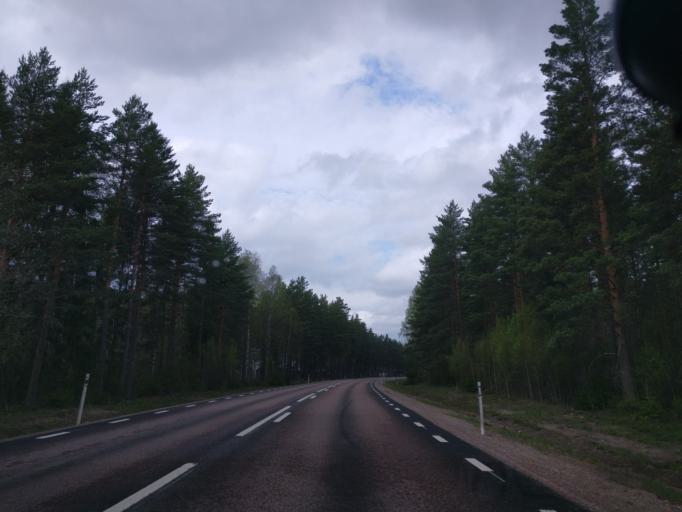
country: SE
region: Vaermland
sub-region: Hagfors Kommun
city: Ekshaerad
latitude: 60.1614
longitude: 13.5044
